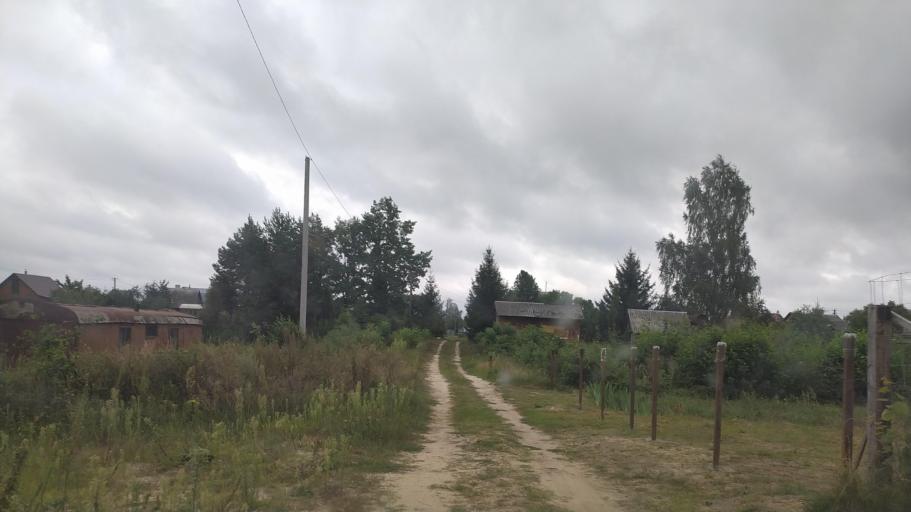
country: BY
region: Brest
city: Byaroza
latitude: 52.5997
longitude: 24.8856
